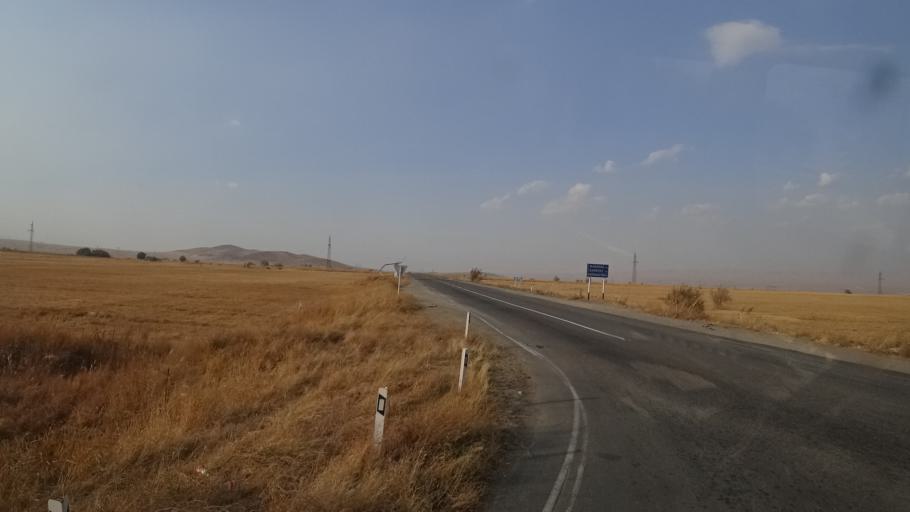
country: KZ
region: Zhambyl
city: Taraz
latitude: 42.7767
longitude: 71.0241
